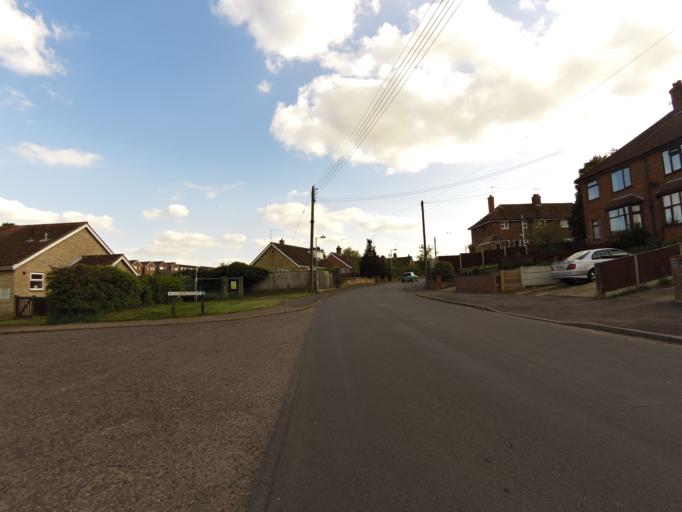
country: GB
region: England
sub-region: Suffolk
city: Beccles
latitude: 52.4483
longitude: 1.5680
